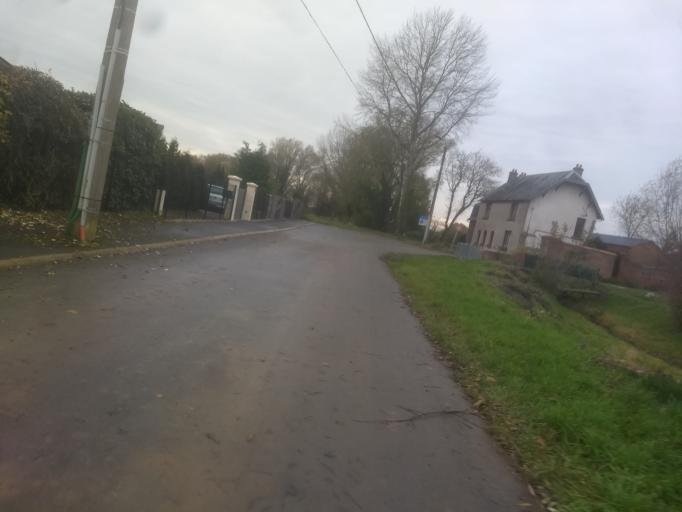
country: FR
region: Nord-Pas-de-Calais
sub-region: Departement du Pas-de-Calais
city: Agny
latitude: 50.2584
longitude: 2.7502
